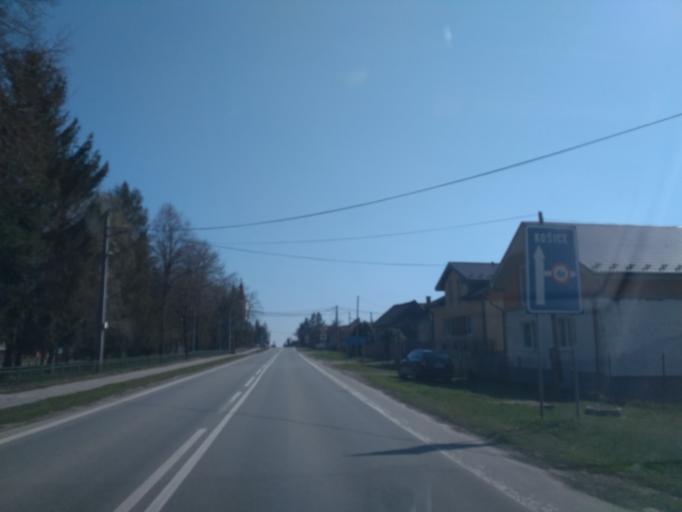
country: SK
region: Kosicky
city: Secovce
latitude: 48.7804
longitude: 21.6857
